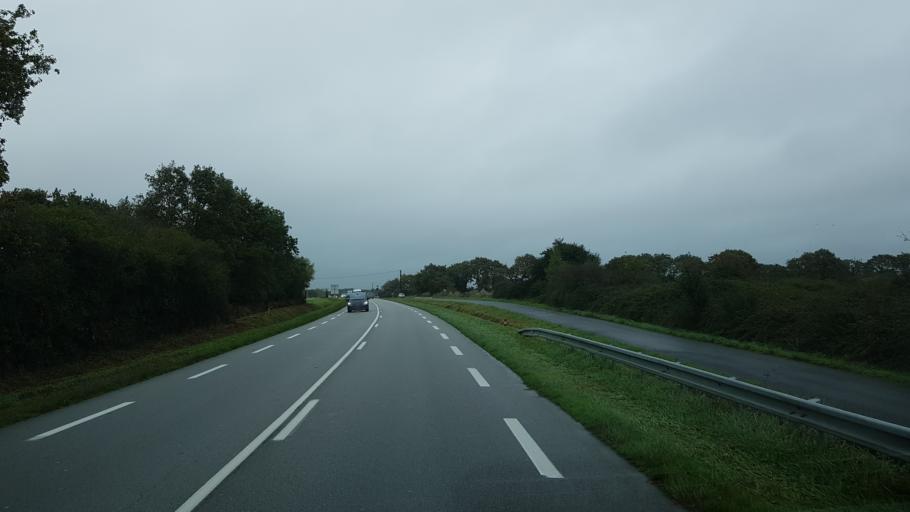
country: FR
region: Brittany
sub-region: Departement du Morbihan
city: Theix
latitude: 47.5948
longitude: -2.6821
